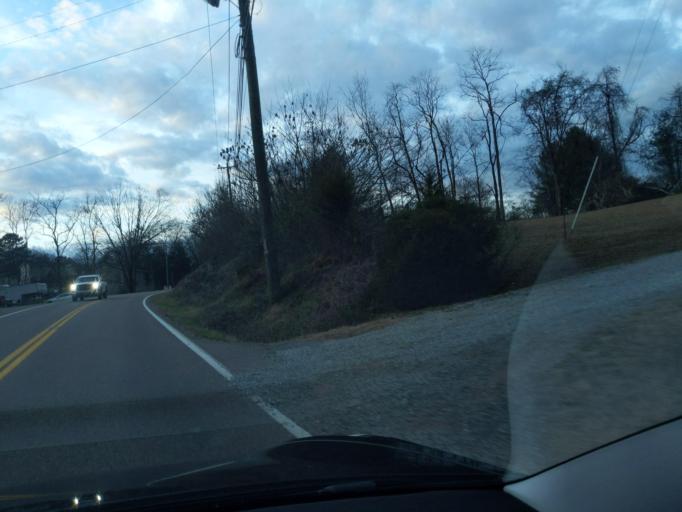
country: US
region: Tennessee
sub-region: Jefferson County
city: Dandridge
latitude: 36.0262
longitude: -83.4077
